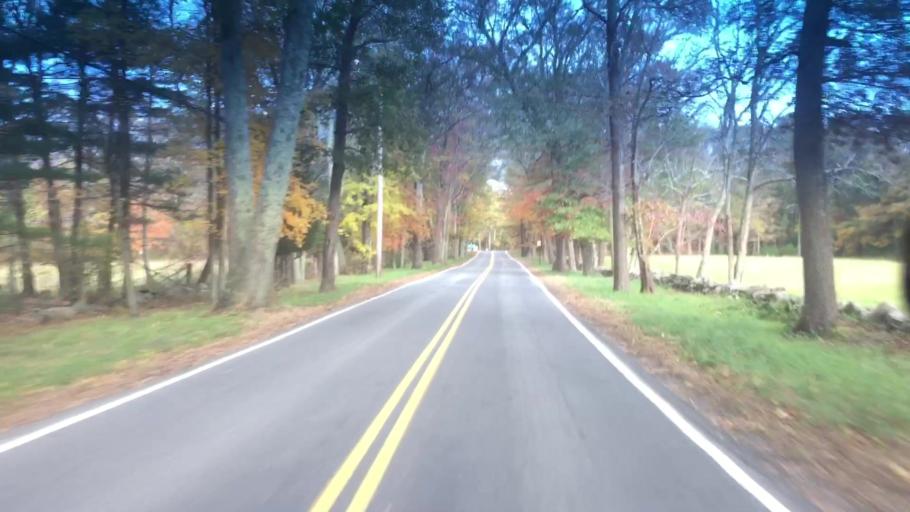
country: US
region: Massachusetts
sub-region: Norfolk County
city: Medfield
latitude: 42.2035
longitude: -71.2779
